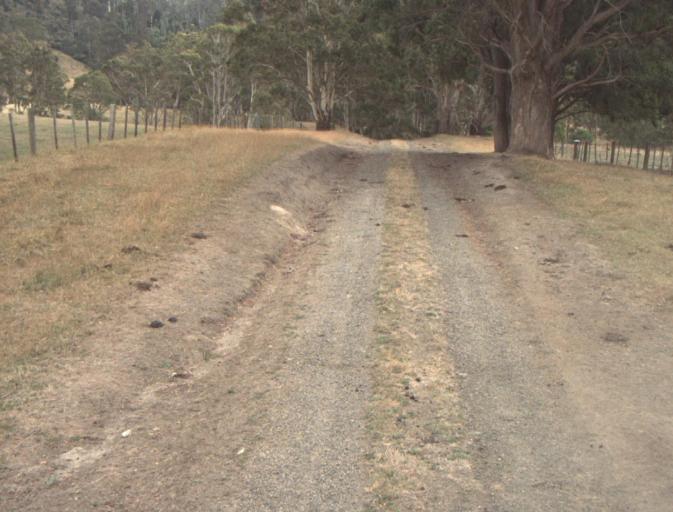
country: AU
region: Tasmania
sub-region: Dorset
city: Scottsdale
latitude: -41.4528
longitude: 147.6012
